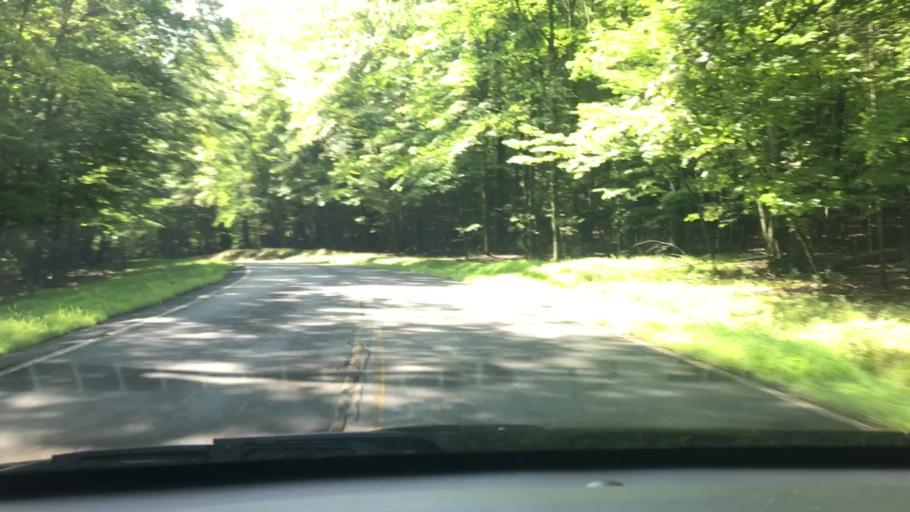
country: US
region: New York
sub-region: Ulster County
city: Shokan
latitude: 41.9329
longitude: -74.2455
